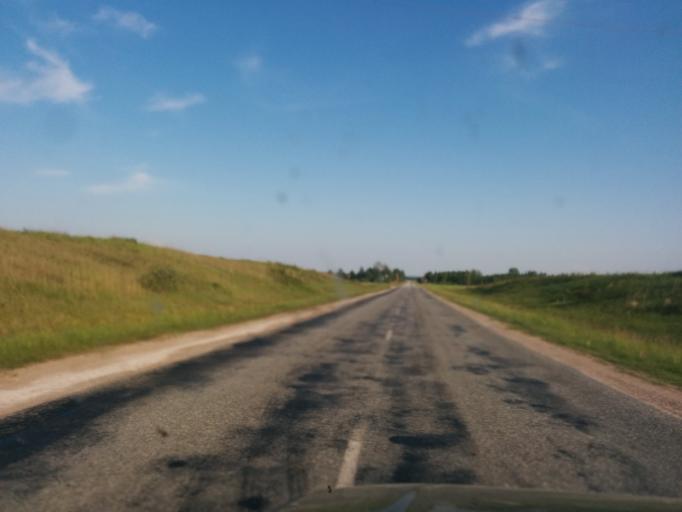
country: LV
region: Talsu Rajons
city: Valdemarpils
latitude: 57.3329
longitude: 22.5150
